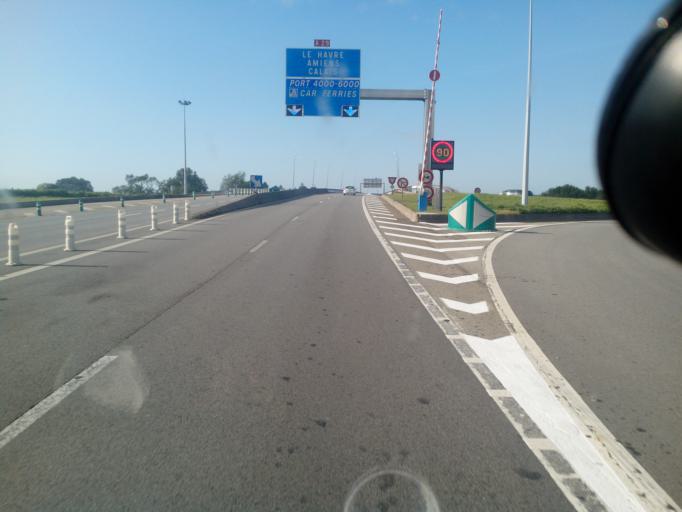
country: FR
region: Lower Normandy
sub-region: Departement du Calvados
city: La Riviere-Saint-Sauveur
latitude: 49.4524
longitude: 0.2715
